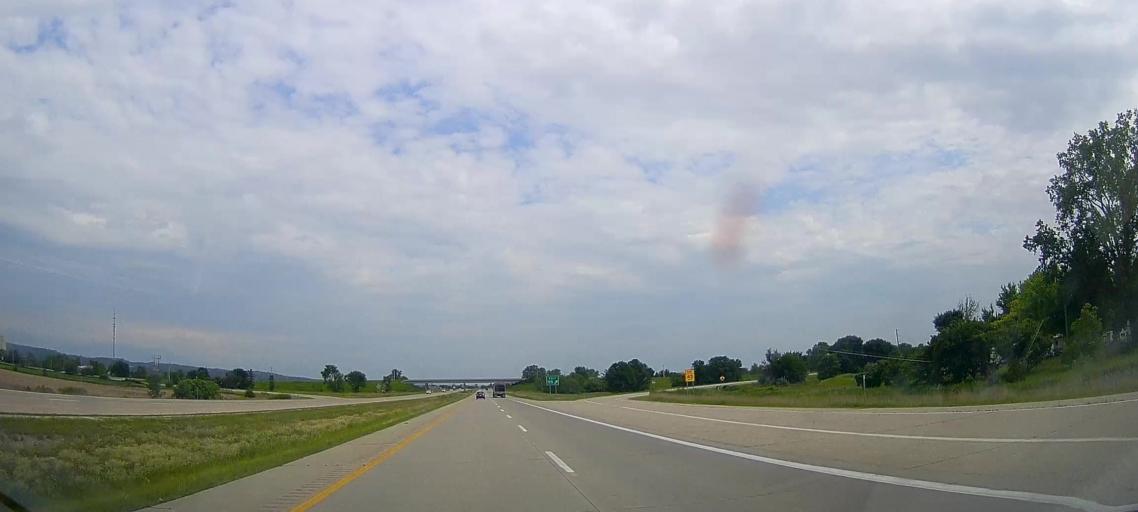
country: US
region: Nebraska
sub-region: Burt County
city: Tekamah
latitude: 41.8043
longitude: -96.0580
